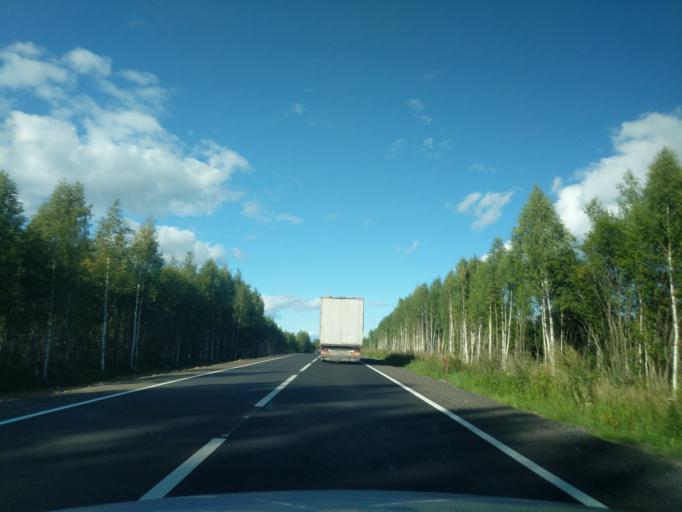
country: RU
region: Kostroma
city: Makar'yev
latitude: 57.9930
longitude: 43.9694
